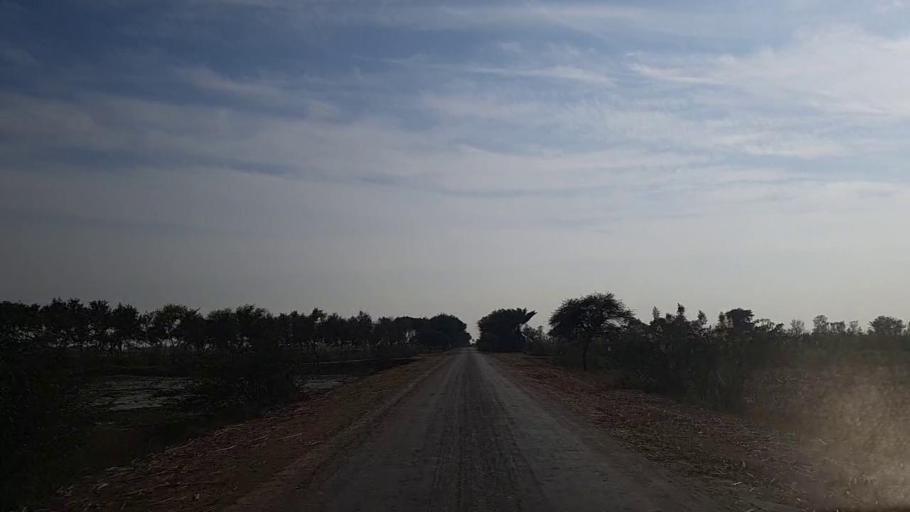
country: PK
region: Sindh
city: Daur
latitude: 26.4646
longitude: 68.4175
